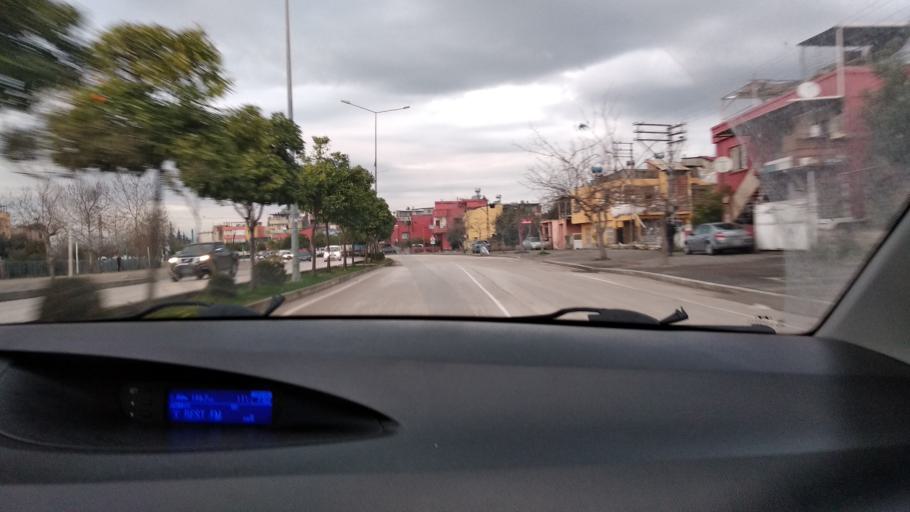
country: TR
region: Adana
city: Yuregir
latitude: 37.0138
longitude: 35.3867
